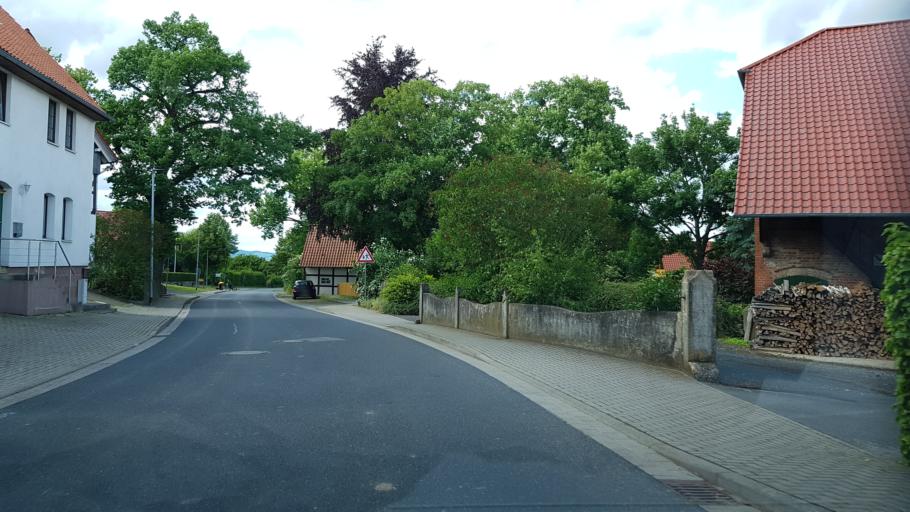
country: DE
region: Lower Saxony
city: Moringen
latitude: 51.7402
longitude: 9.8807
